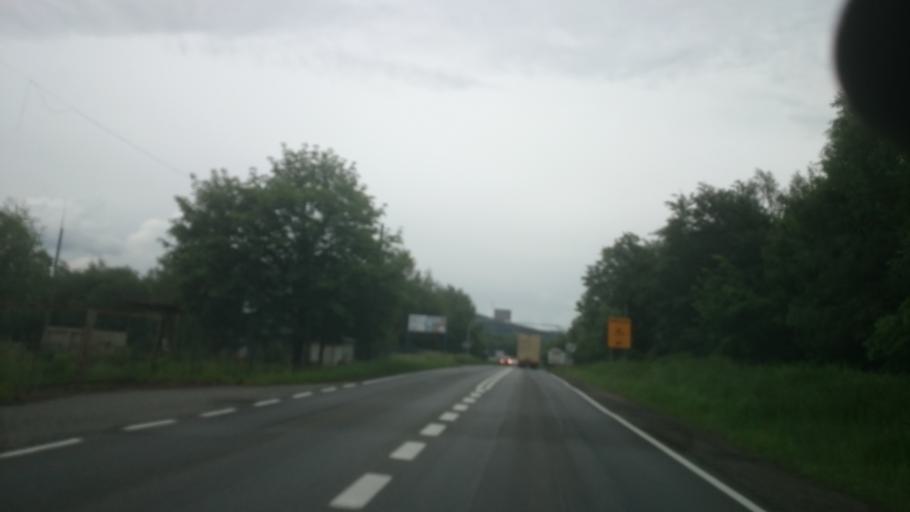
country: PL
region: Lower Silesian Voivodeship
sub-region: Powiat klodzki
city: Klodzko
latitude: 50.4333
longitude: 16.6739
